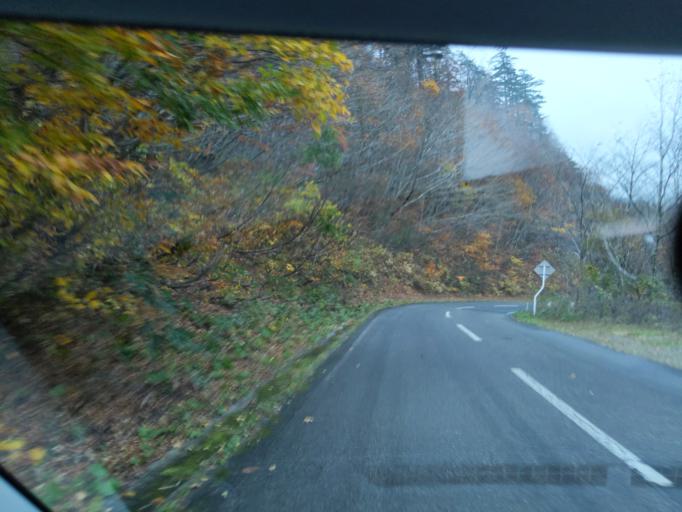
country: JP
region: Iwate
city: Mizusawa
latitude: 39.1213
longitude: 140.8337
